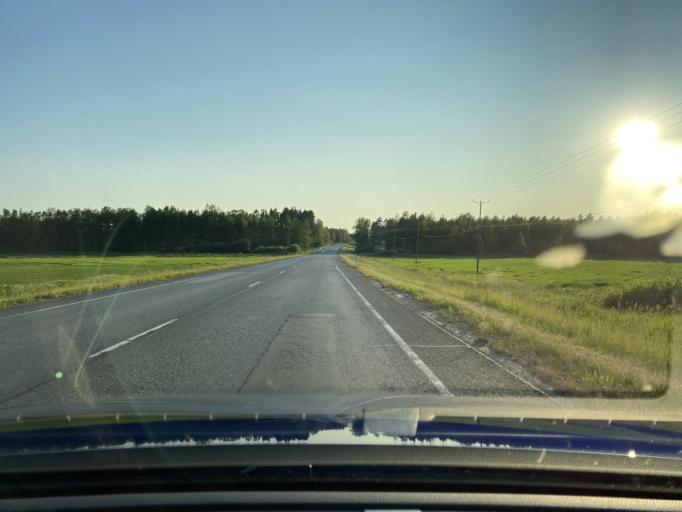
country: FI
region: Haeme
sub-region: Forssa
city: Tammela
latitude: 60.8253
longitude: 23.9729
